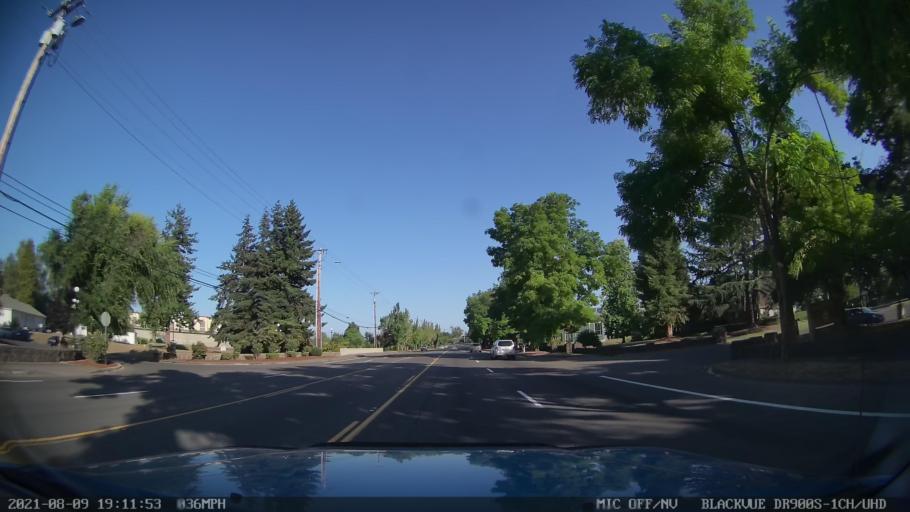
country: US
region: Oregon
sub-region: Marion County
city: Four Corners
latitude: 44.9317
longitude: -123.0081
